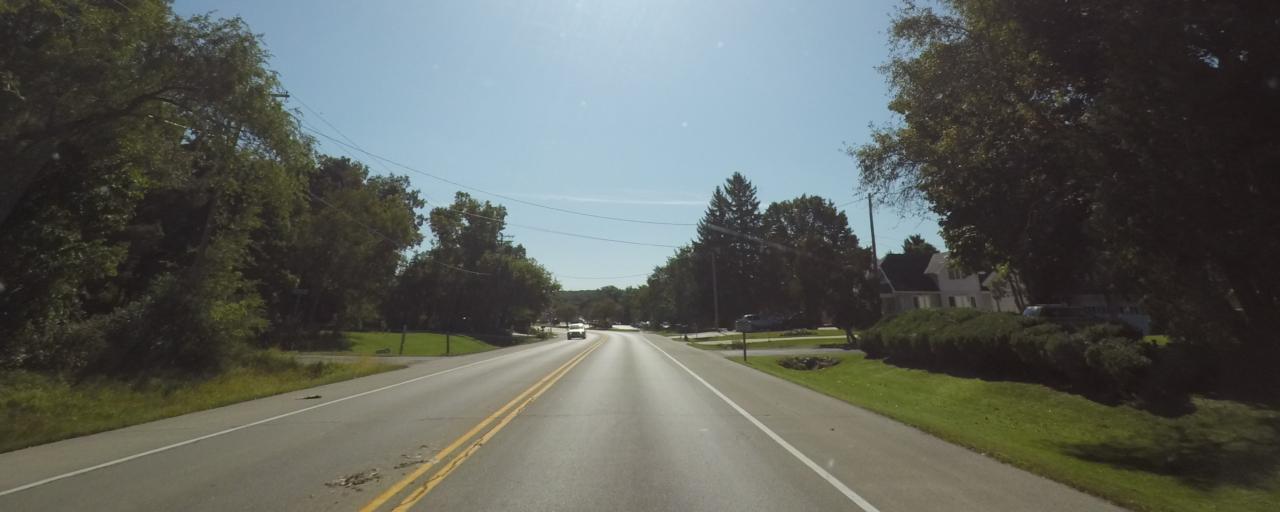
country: US
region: Wisconsin
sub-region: Waukesha County
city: Waukesha
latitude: 42.9989
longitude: -88.2109
